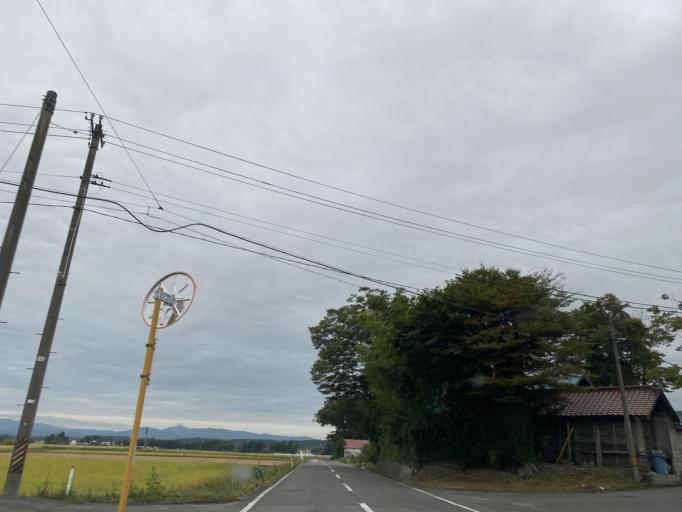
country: JP
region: Fukushima
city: Koriyama
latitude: 37.3535
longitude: 140.2629
